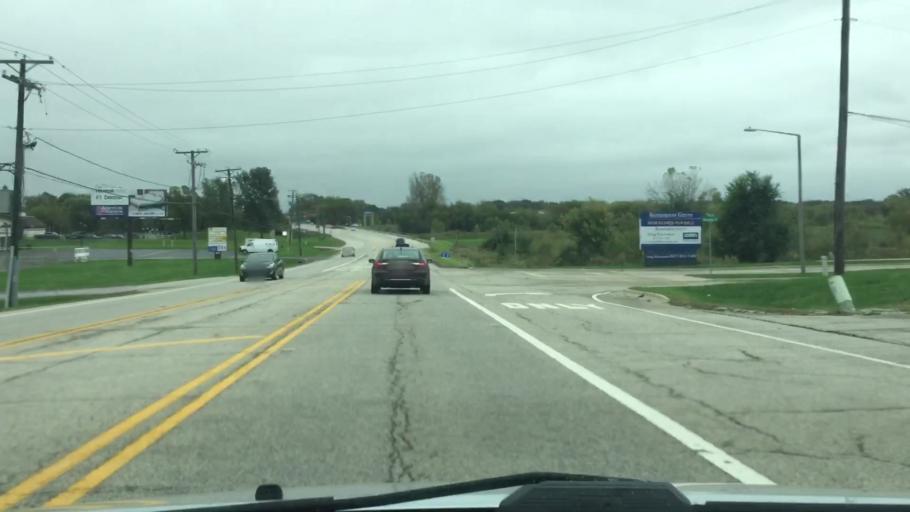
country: US
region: Illinois
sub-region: McHenry County
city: McCullom Lake
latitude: 42.3758
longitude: -88.2694
